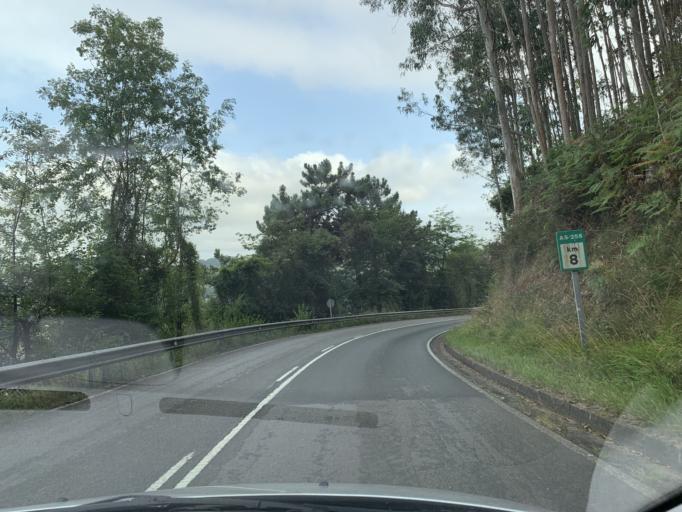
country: ES
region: Asturias
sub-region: Province of Asturias
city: Villaviciosa
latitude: 43.5102
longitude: -5.4268
